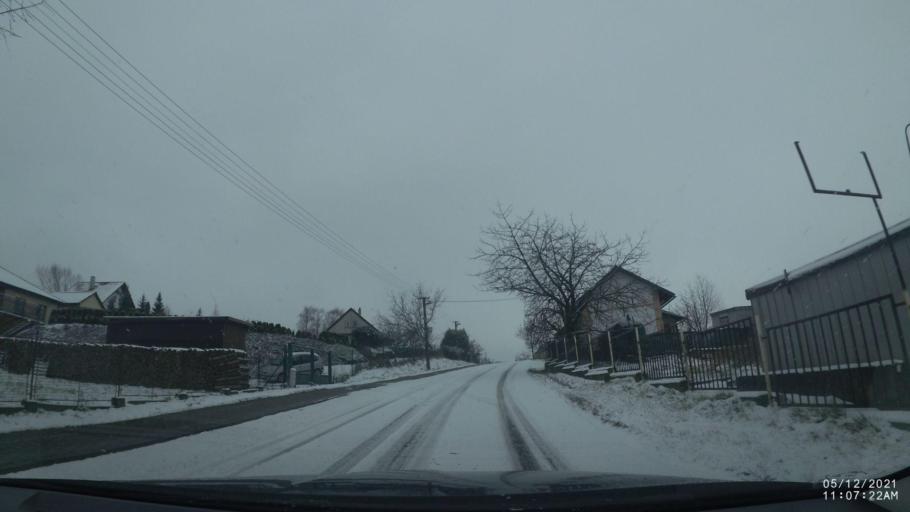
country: CZ
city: Solnice
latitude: 50.1787
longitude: 16.2238
